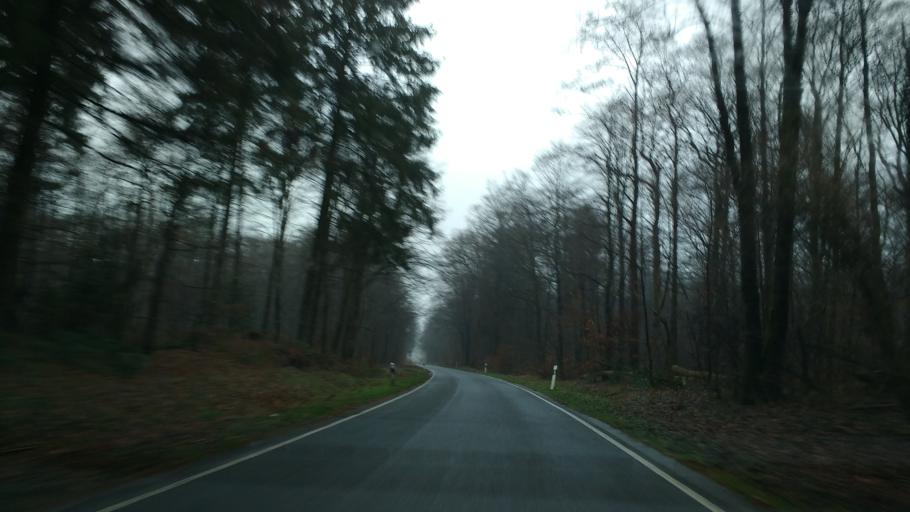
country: DE
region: Schleswig-Holstein
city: Nindorf
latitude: 54.1463
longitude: 9.6974
